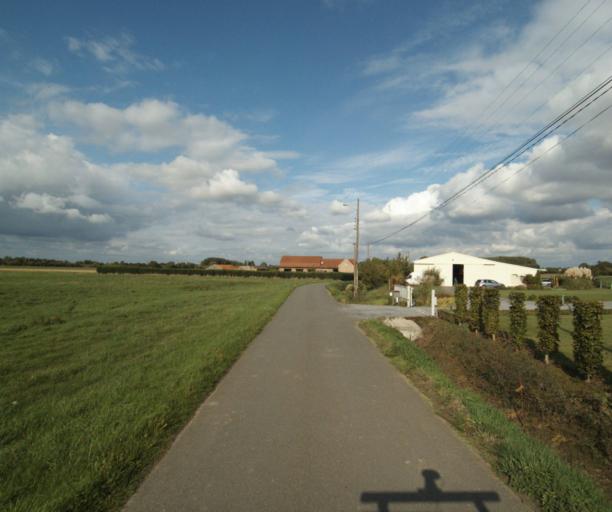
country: FR
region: Nord-Pas-de-Calais
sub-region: Departement du Nord
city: Ennetieres-en-Weppes
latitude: 50.6389
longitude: 2.9237
